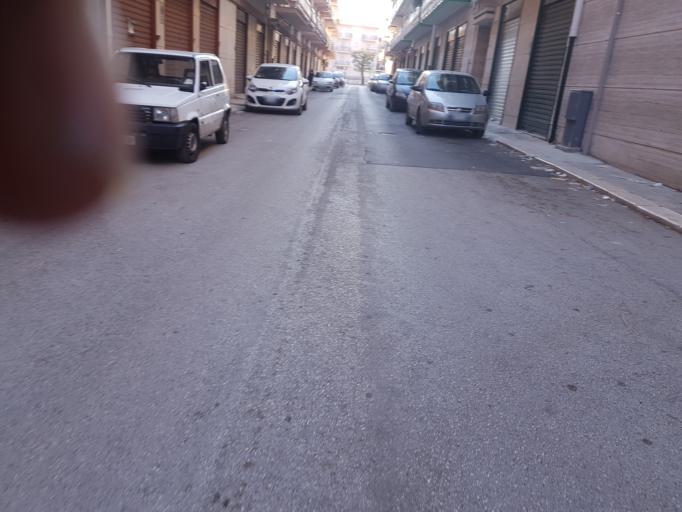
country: IT
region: Apulia
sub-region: Provincia di Bari
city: Corato
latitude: 41.1494
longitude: 16.4052
